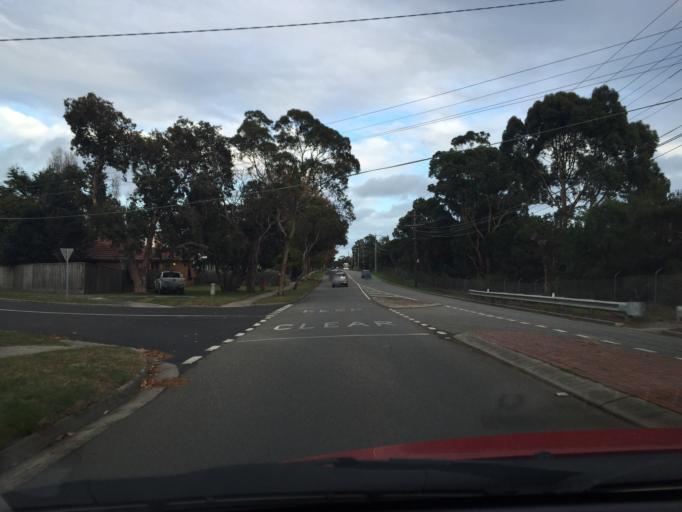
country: AU
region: Victoria
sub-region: Frankston
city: Frankston East
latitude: -38.1327
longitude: 145.1408
